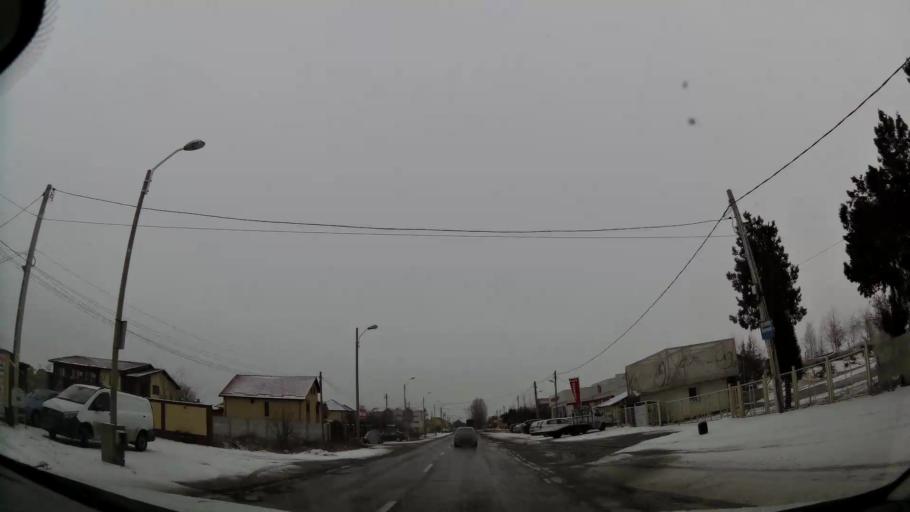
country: RO
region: Dambovita
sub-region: Comuna Ulmi
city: Ulmi
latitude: 44.9031
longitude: 25.4976
